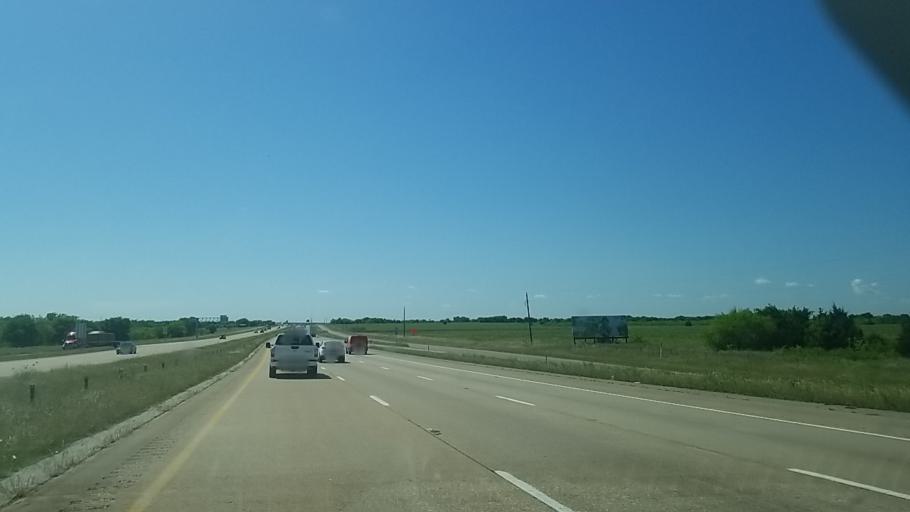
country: US
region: Texas
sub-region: Ellis County
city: Ennis
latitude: 32.2880
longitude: -96.5479
